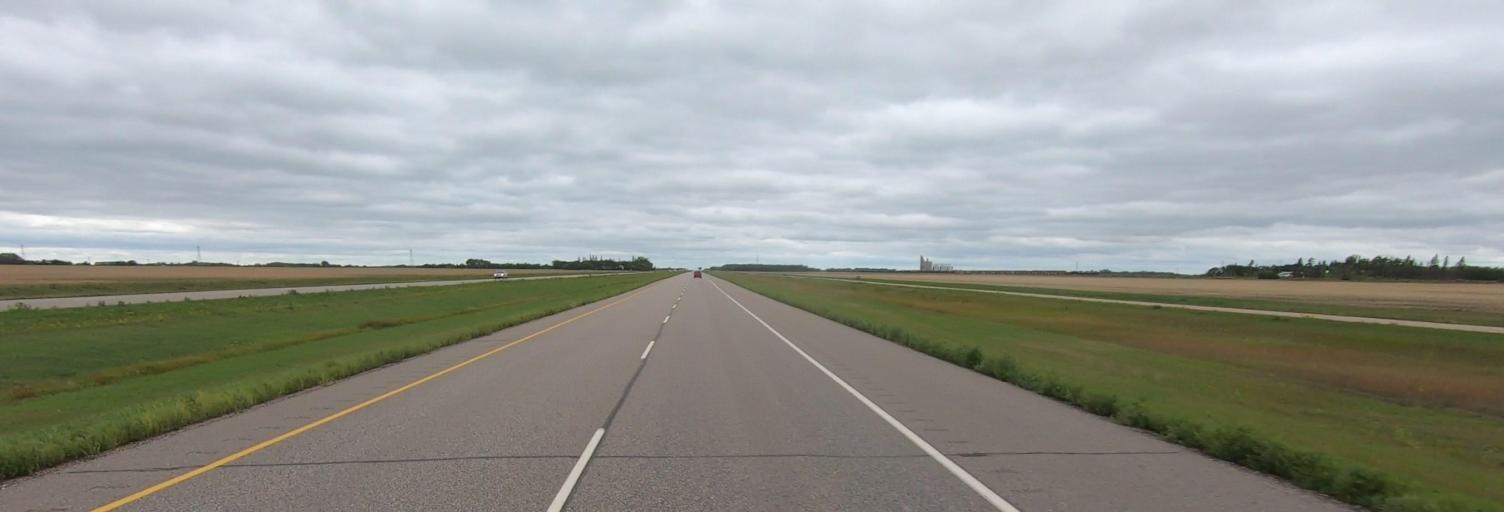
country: CA
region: Manitoba
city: Portage la Prairie
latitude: 49.9752
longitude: -98.5178
